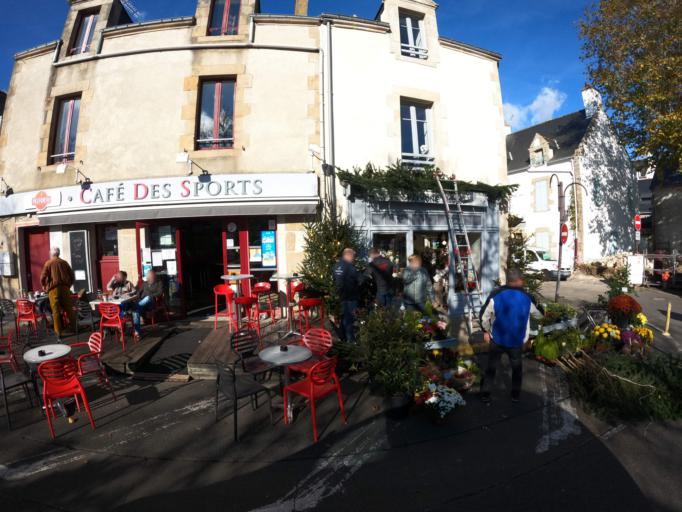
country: FR
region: Pays de la Loire
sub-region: Departement de la Loire-Atlantique
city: Le Croisic
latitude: 47.2932
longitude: -2.5101
